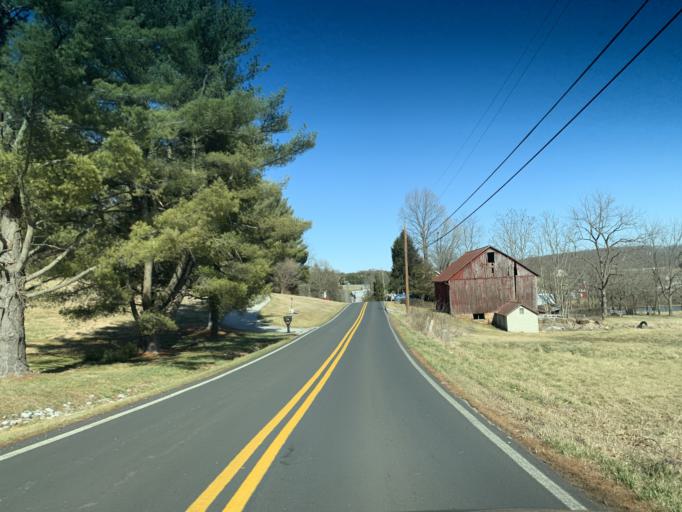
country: US
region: Maryland
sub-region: Carroll County
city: Manchester
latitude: 39.6165
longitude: -76.8978
